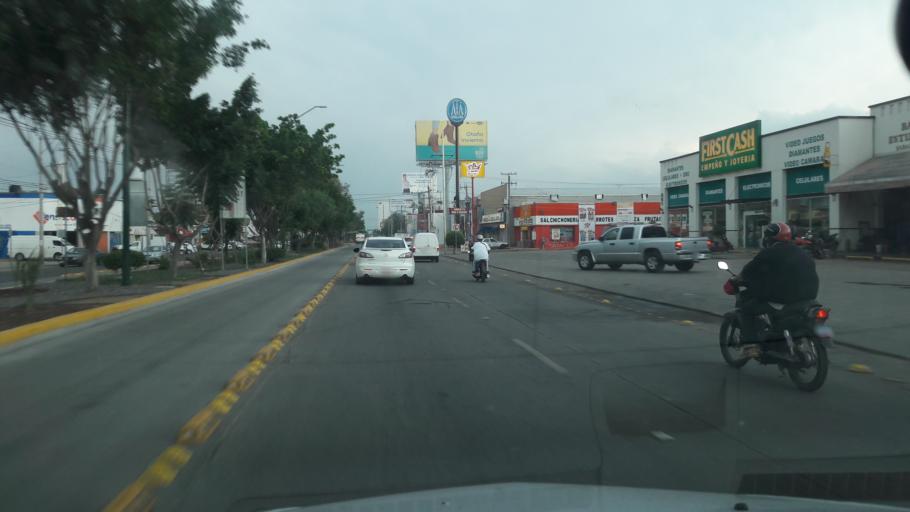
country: MX
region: Guanajuato
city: Leon
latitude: 21.1237
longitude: -101.6489
